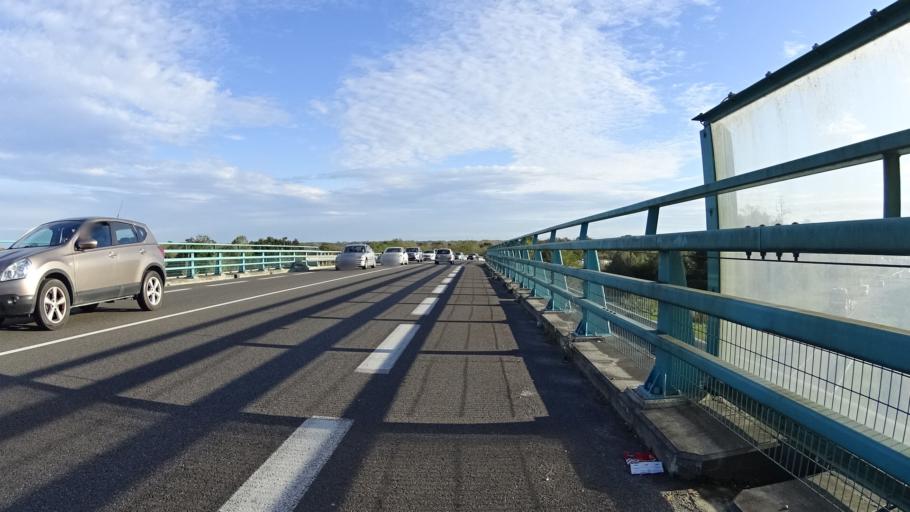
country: FR
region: Aquitaine
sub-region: Departement des Landes
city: Saint-Paul-les-Dax
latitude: 43.7278
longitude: -1.0364
